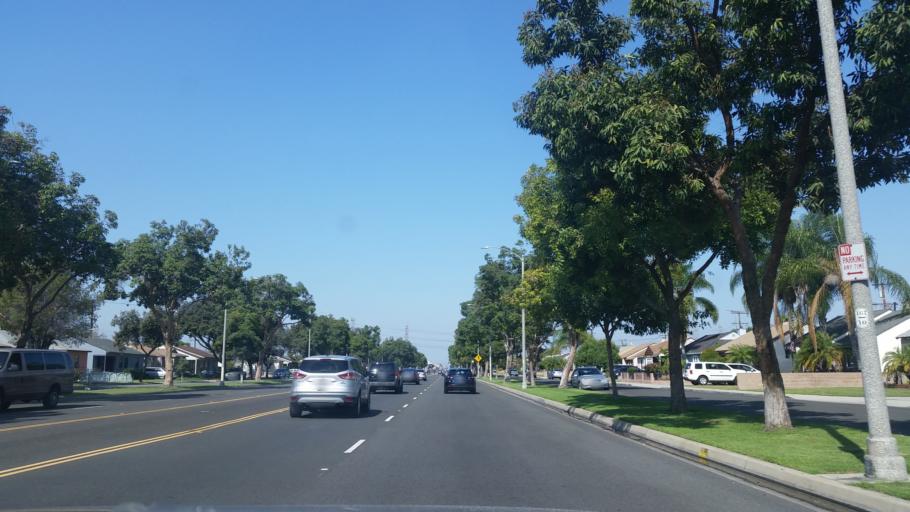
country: US
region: California
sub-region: Los Angeles County
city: Lakewood
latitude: 33.8627
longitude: -118.1250
